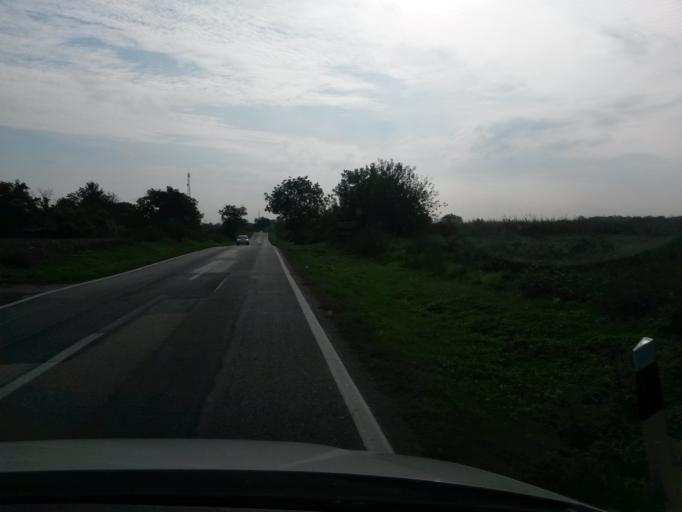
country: HR
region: Vukovarsko-Srijemska
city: Lovas
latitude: 45.2640
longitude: 19.1612
